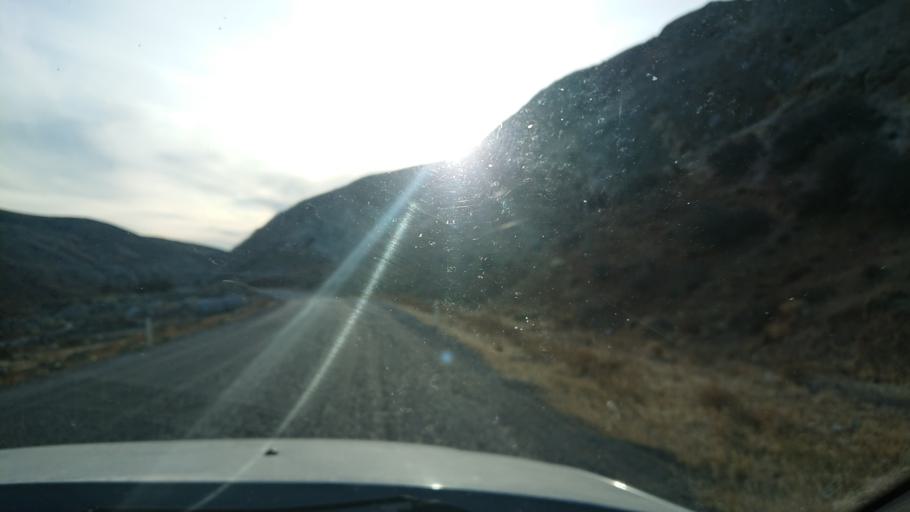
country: TR
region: Ankara
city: Sereflikochisar
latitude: 38.7564
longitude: 33.6944
